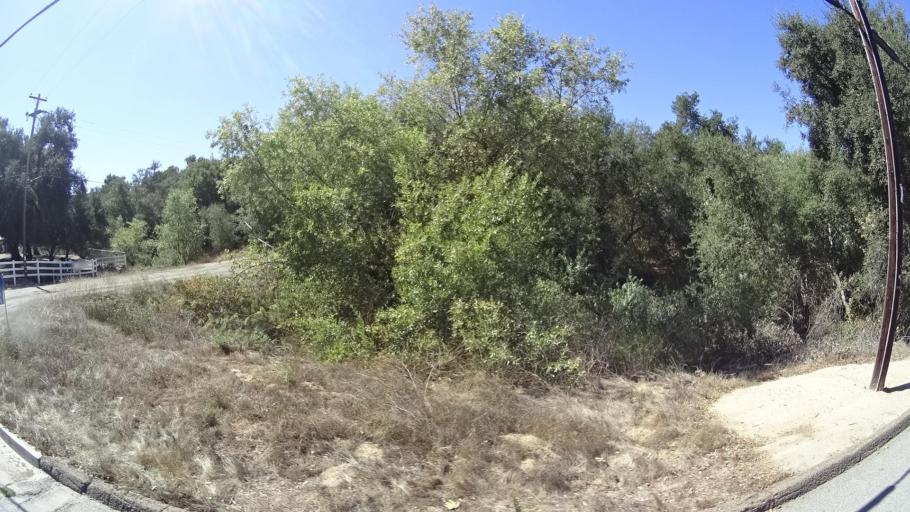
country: US
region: California
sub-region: San Diego County
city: Alpine
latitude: 32.7488
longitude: -116.7576
